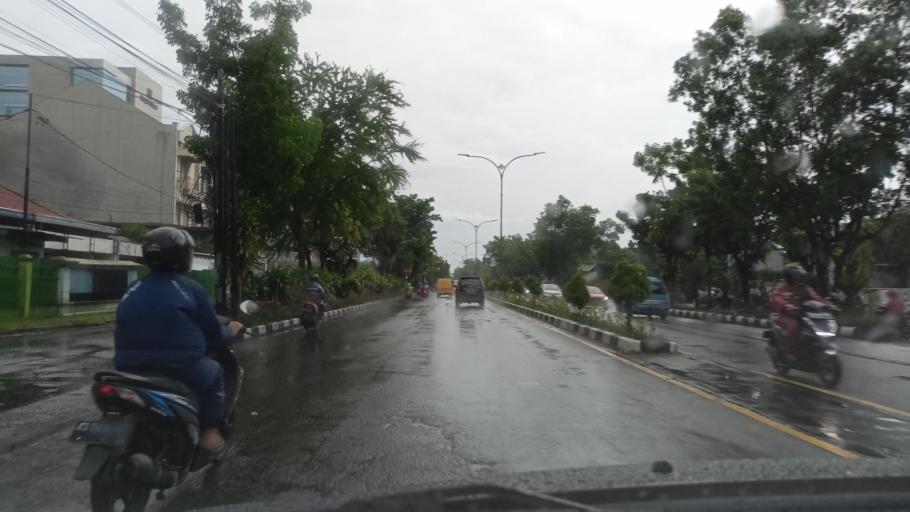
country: ID
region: Central Java
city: Colomadu
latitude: -7.5502
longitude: 110.7885
